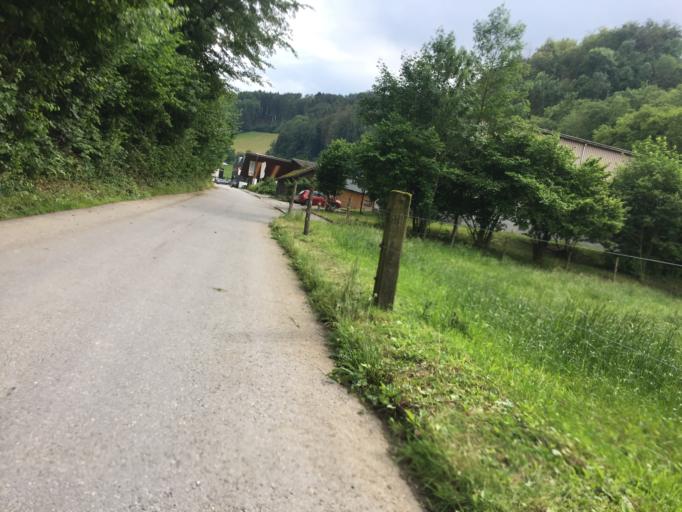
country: CH
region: Bern
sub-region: Bern-Mittelland District
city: Stettlen
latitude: 46.9551
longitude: 7.5120
